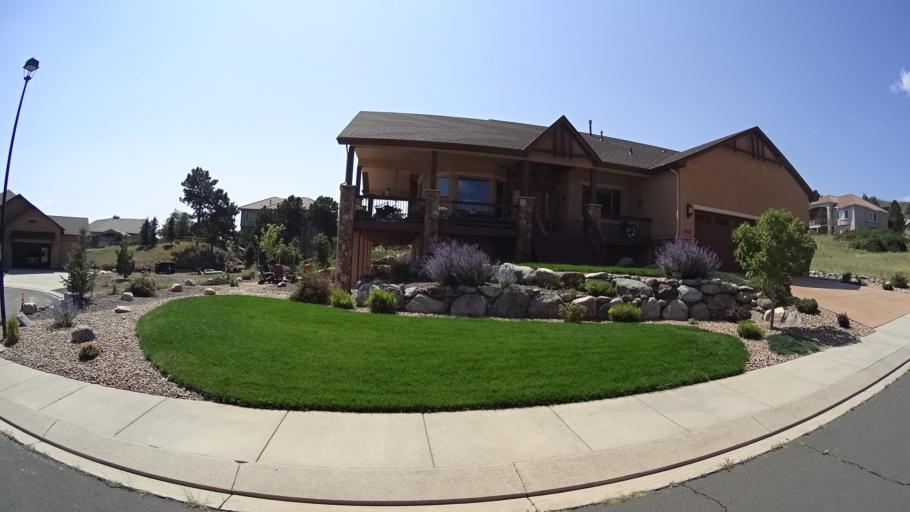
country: US
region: Colorado
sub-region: El Paso County
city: Manitou Springs
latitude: 38.9235
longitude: -104.8823
